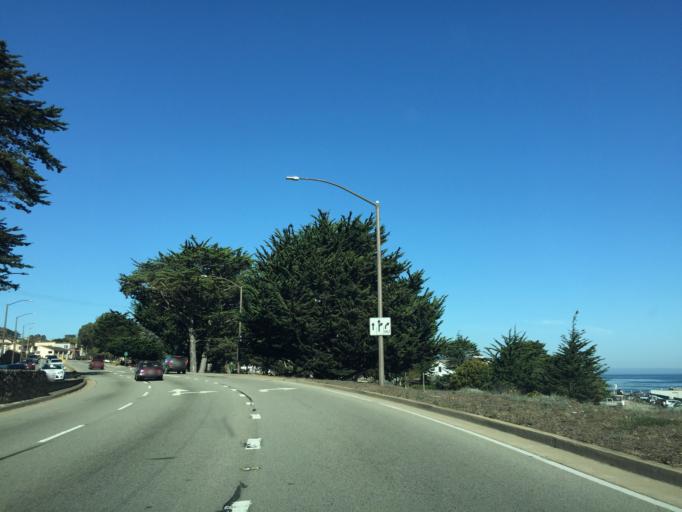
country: US
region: California
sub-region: Monterey County
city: Monterey
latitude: 36.6074
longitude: -121.8947
